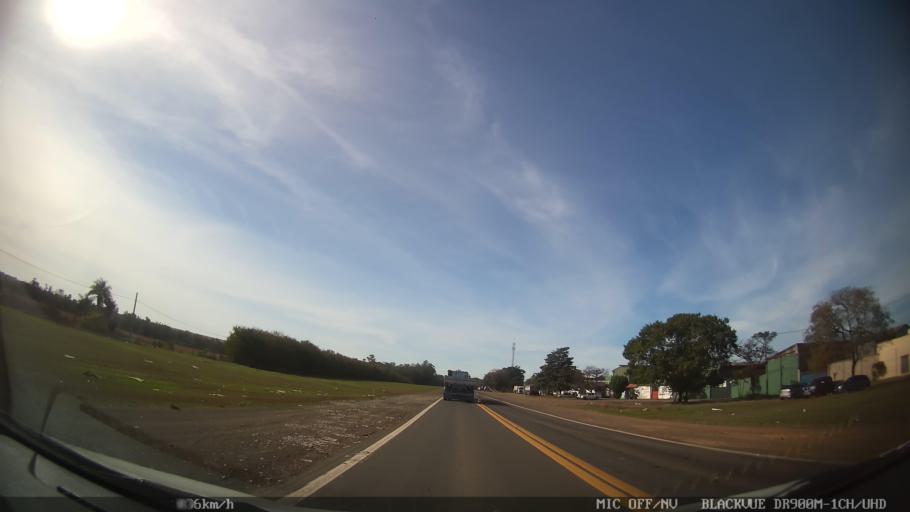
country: BR
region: Sao Paulo
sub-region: Rio Das Pedras
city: Rio das Pedras
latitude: -22.7942
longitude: -47.6178
